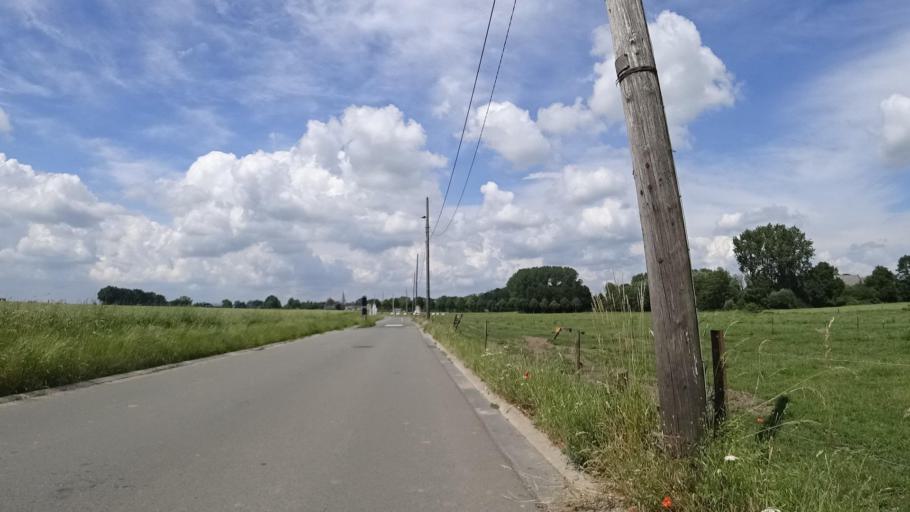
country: BE
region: Wallonia
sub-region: Province du Brabant Wallon
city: Walhain-Saint-Paul
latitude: 50.6304
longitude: 4.7225
